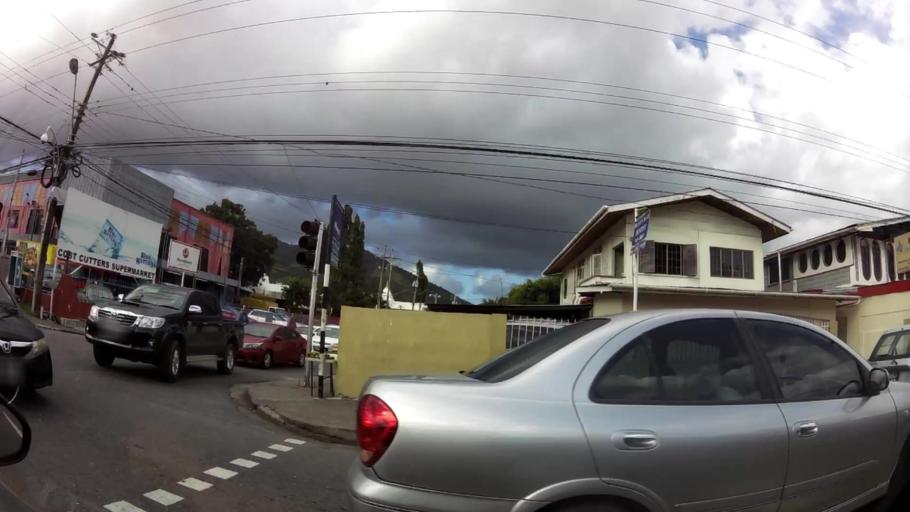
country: TT
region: Tunapuna/Piarco
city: Paradise
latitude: 10.6458
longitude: -61.3718
